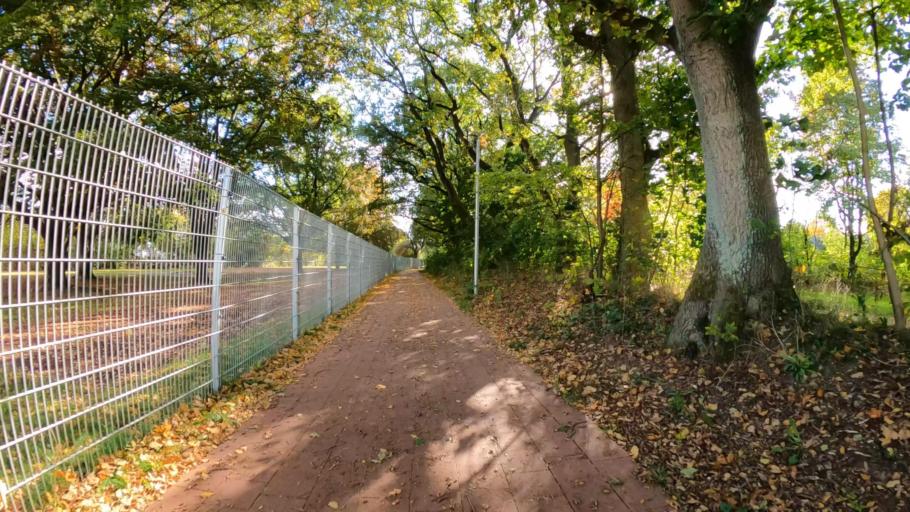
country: DE
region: Schleswig-Holstein
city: Ahrensburg
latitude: 53.6719
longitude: 10.2225
